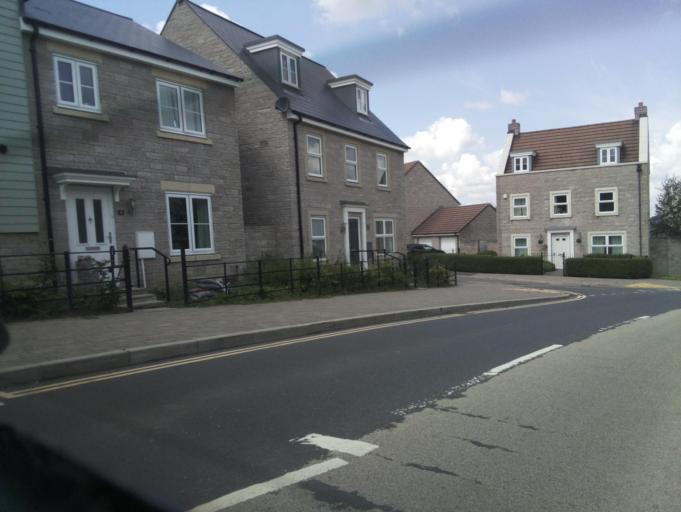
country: GB
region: England
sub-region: Wiltshire
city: Purton
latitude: 51.5809
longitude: -1.8333
